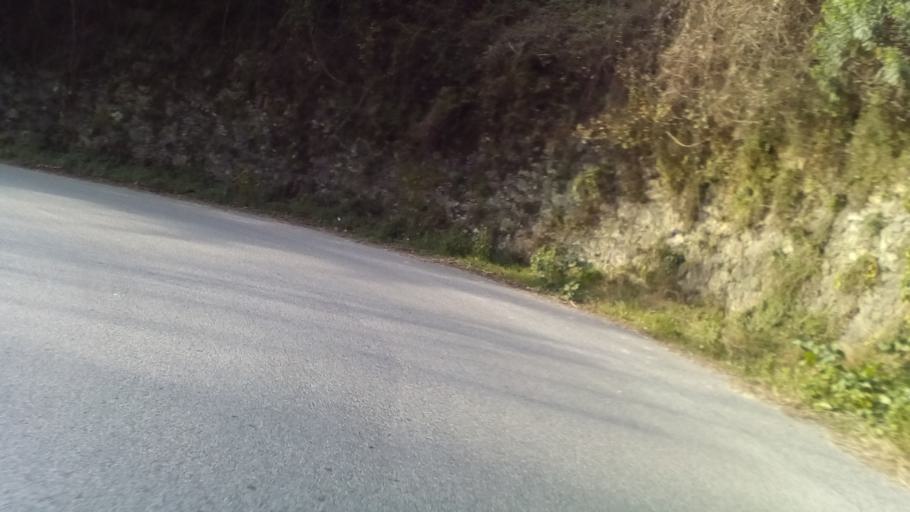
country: IT
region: Tuscany
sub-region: Provincia di Massa-Carrara
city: Carrara
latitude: 44.0837
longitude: 10.1107
